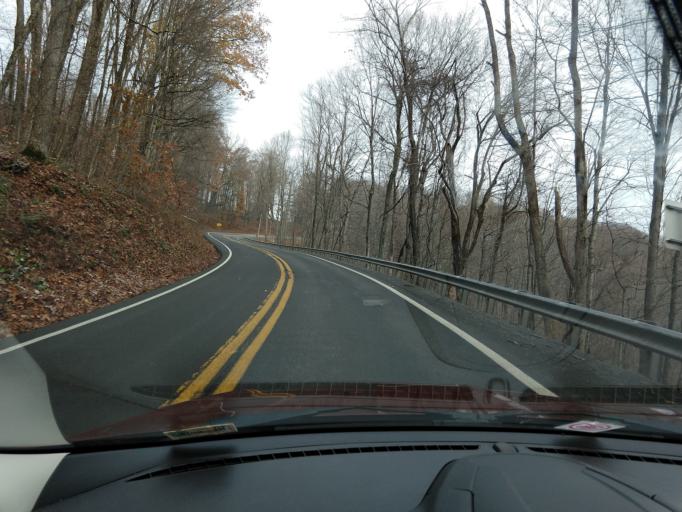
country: US
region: West Virginia
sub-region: Nicholas County
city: Craigsville
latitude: 38.1847
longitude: -80.6852
